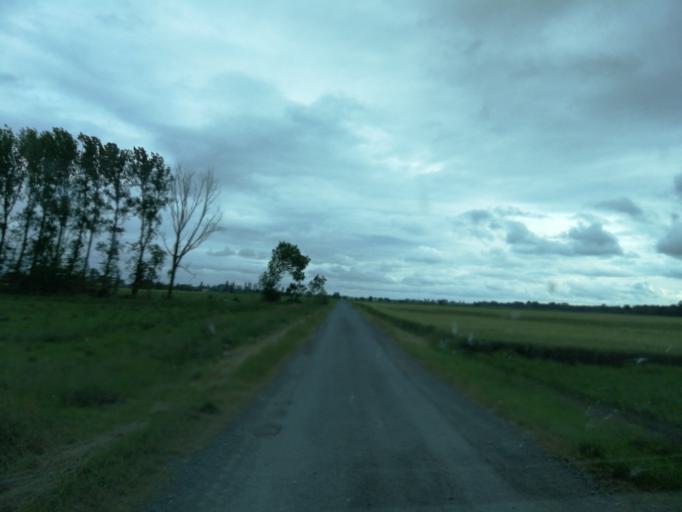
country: FR
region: Pays de la Loire
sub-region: Departement de la Vendee
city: Vix
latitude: 46.3661
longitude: -0.9341
